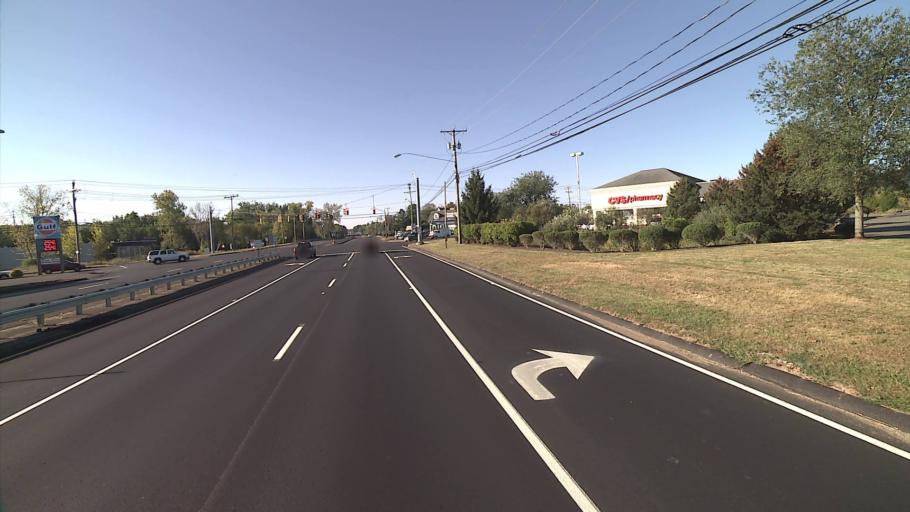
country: US
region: Connecticut
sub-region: Hartford County
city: Kensington
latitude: 41.6420
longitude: -72.7332
